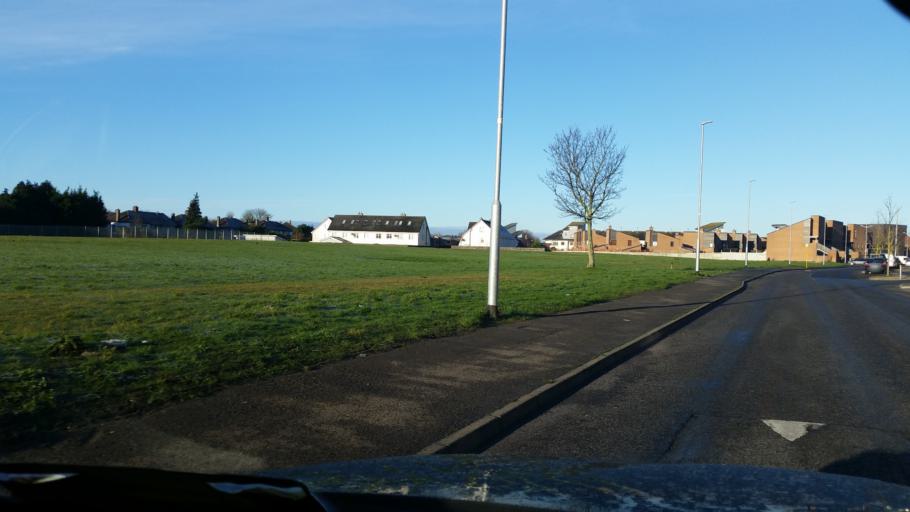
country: IE
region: Leinster
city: Ballymun
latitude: 53.3955
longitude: -6.2727
